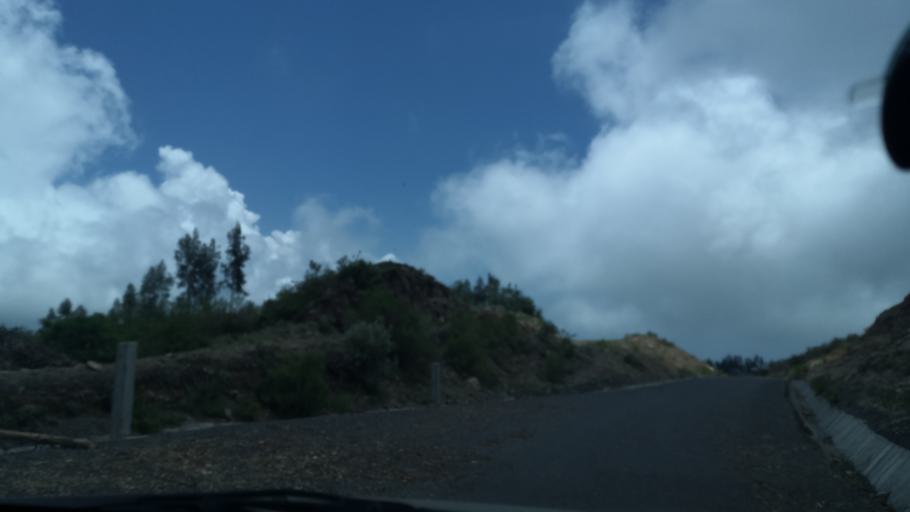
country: ET
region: Amhara
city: Kemise
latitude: 10.3656
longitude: 39.8303
